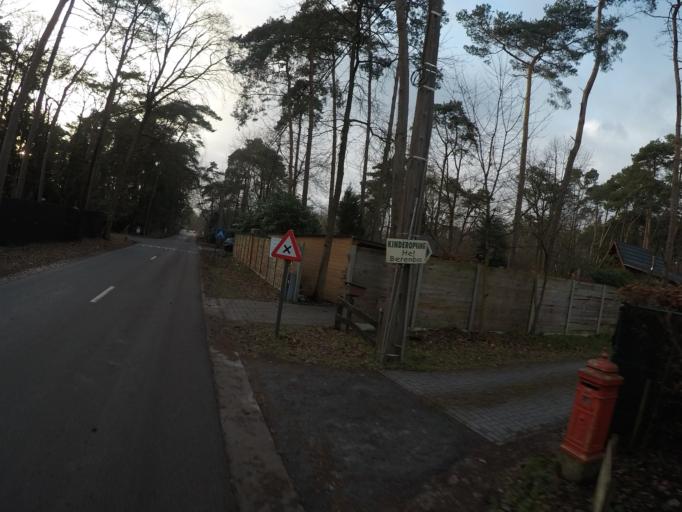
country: BE
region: Flanders
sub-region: Provincie Antwerpen
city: Brecht
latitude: 51.3221
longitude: 4.5718
